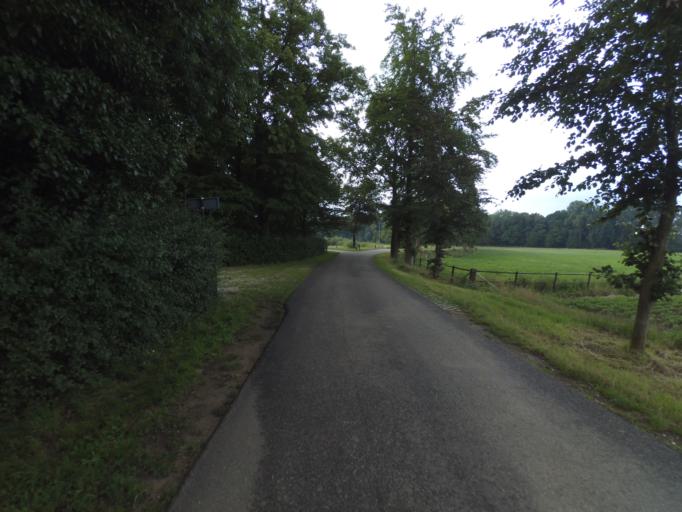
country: NL
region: Limburg
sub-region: Gemeente Maasgouw
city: Maasbracht
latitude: 51.1599
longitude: 5.9219
